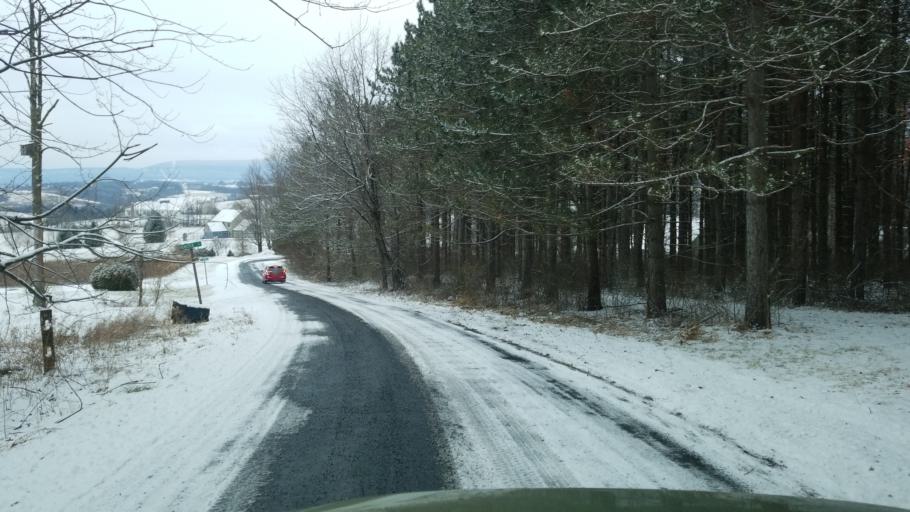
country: US
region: Pennsylvania
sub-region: Centre County
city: Centre Hall
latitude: 40.7732
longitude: -77.6704
